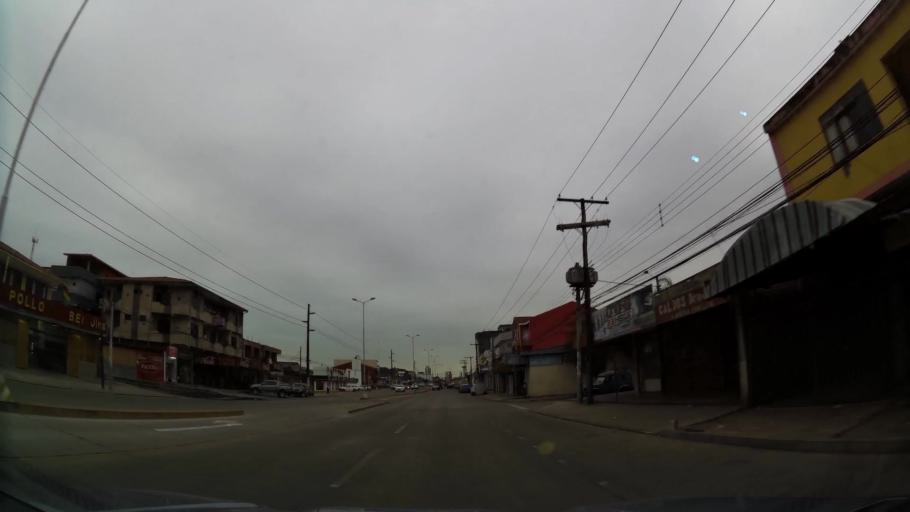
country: BO
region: Santa Cruz
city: Santa Cruz de la Sierra
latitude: -17.7800
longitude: -63.2039
